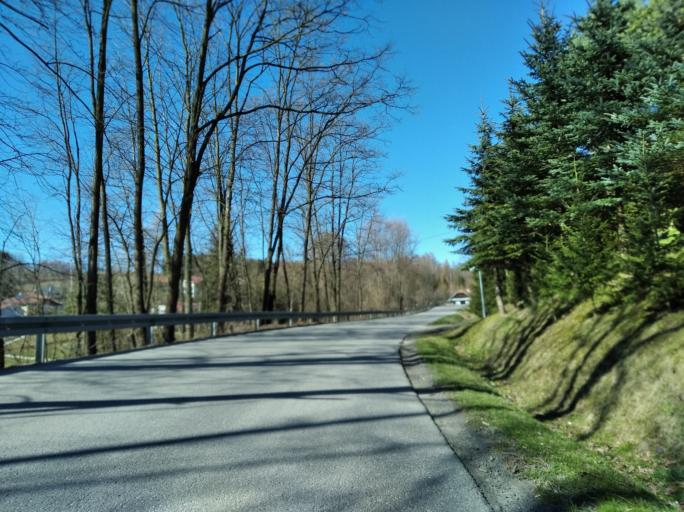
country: PL
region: Subcarpathian Voivodeship
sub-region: Powiat strzyzowski
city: Wisniowa
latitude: 49.8900
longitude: 21.6660
